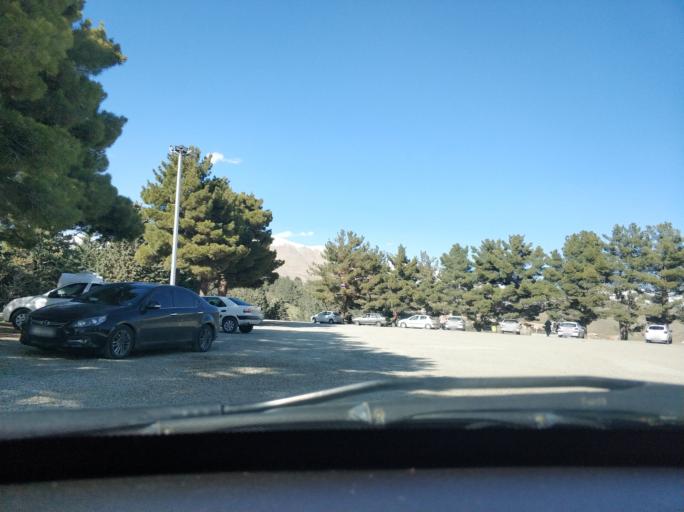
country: IR
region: Tehran
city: Tajrish
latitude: 35.7998
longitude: 51.5672
